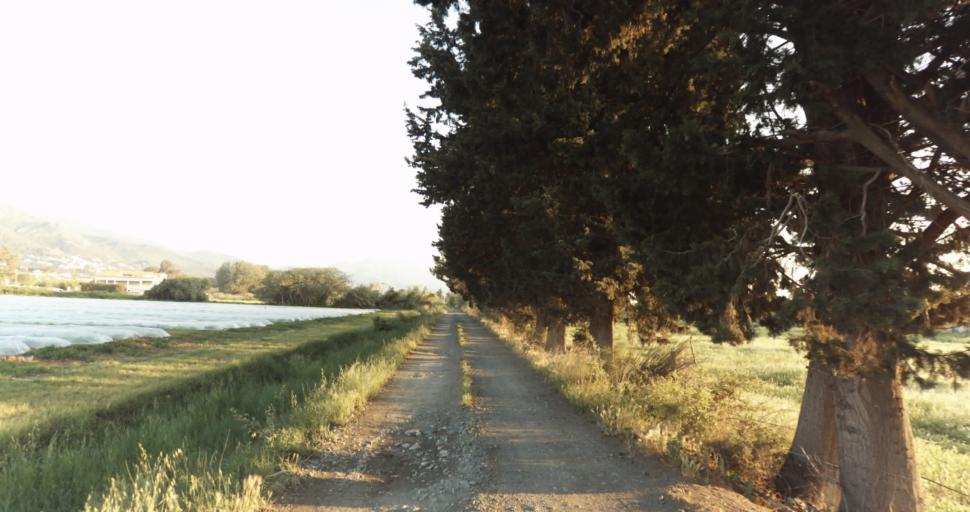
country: FR
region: Corsica
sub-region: Departement de la Haute-Corse
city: Biguglia
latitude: 42.6114
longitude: 9.4470
